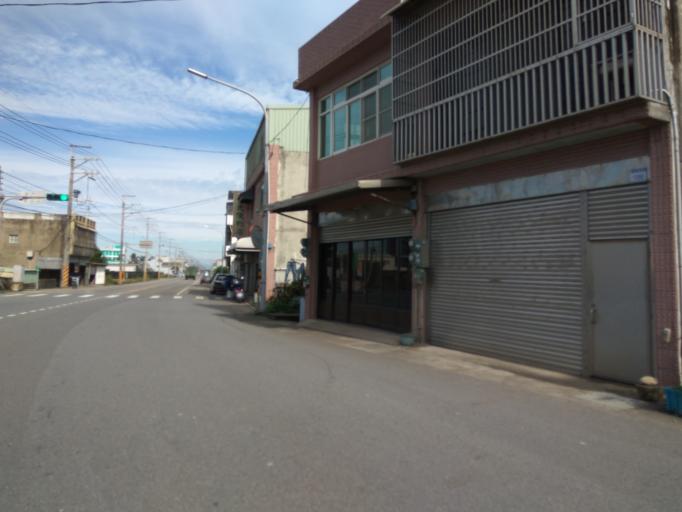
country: TW
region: Taiwan
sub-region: Hsinchu
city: Zhubei
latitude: 24.9902
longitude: 121.1018
